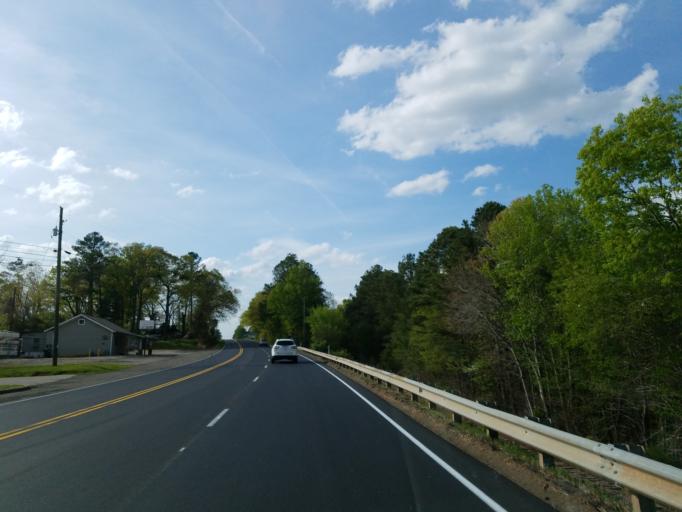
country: US
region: Georgia
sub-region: Pickens County
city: Jasper
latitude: 34.4517
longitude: -84.4051
